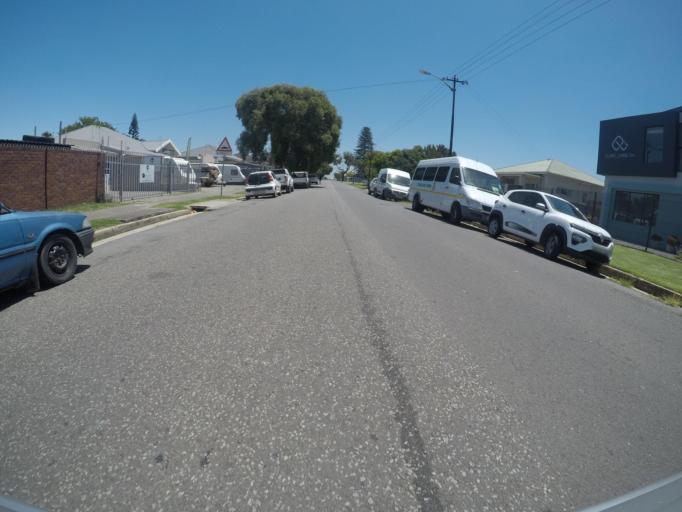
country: ZA
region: Eastern Cape
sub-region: Buffalo City Metropolitan Municipality
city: East London
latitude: -32.9897
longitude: 27.9101
